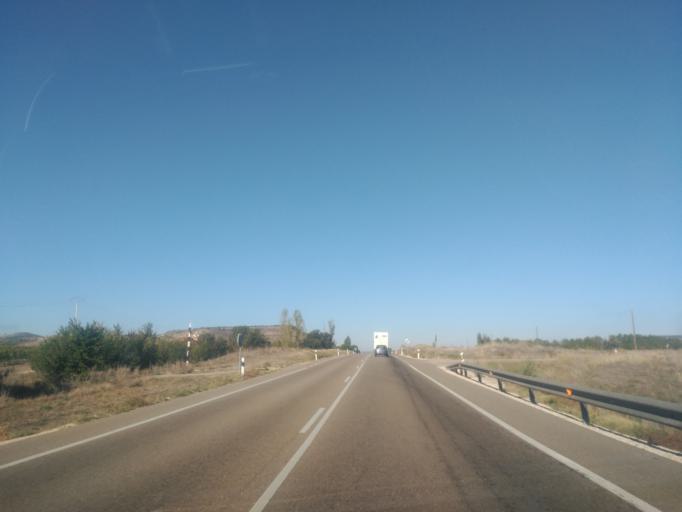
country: ES
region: Castille and Leon
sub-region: Provincia de Valladolid
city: Manzanillo
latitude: 41.6148
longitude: -4.1874
